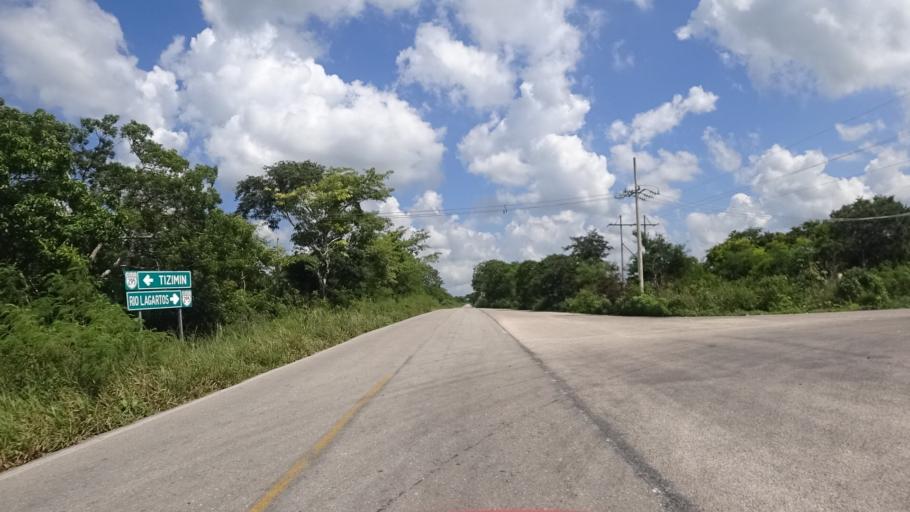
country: MX
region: Yucatan
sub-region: Panaba
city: Loche
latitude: 21.3802
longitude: -88.1427
